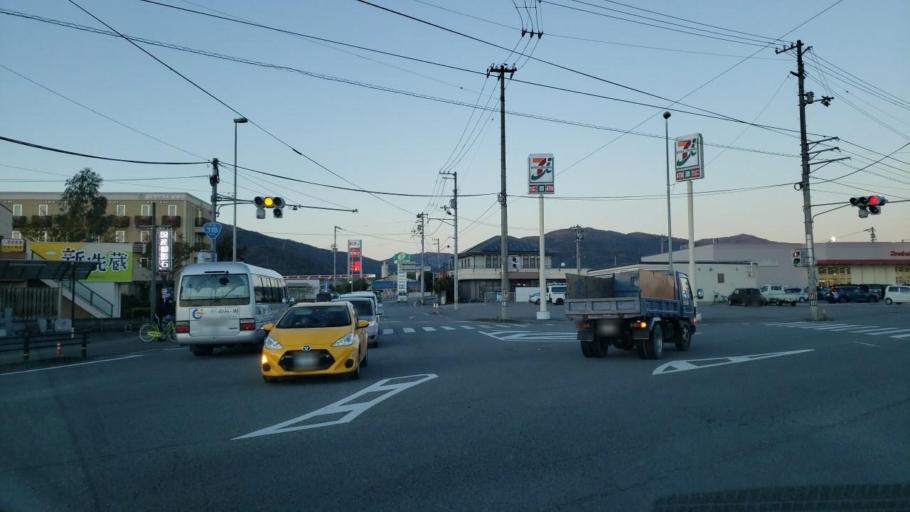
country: JP
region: Tokushima
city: Kamojimacho-jogejima
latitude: 34.1019
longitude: 134.3452
